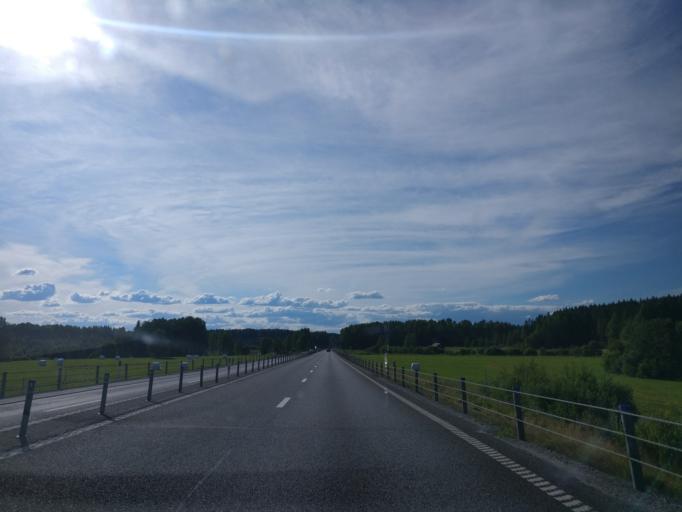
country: SE
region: Vaermland
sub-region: Arvika Kommun
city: Arvika
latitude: 59.6523
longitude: 12.6670
